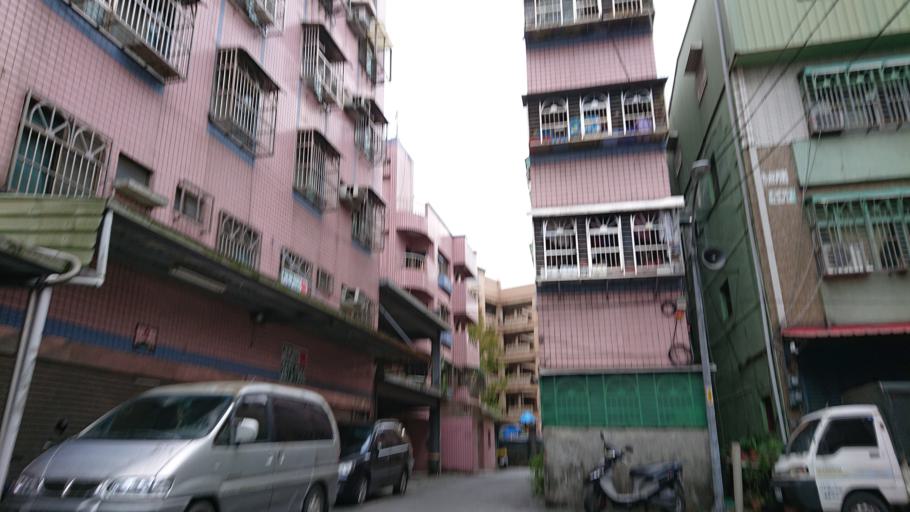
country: TW
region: Taiwan
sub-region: Taoyuan
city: Taoyuan
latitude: 24.9264
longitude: 121.3745
